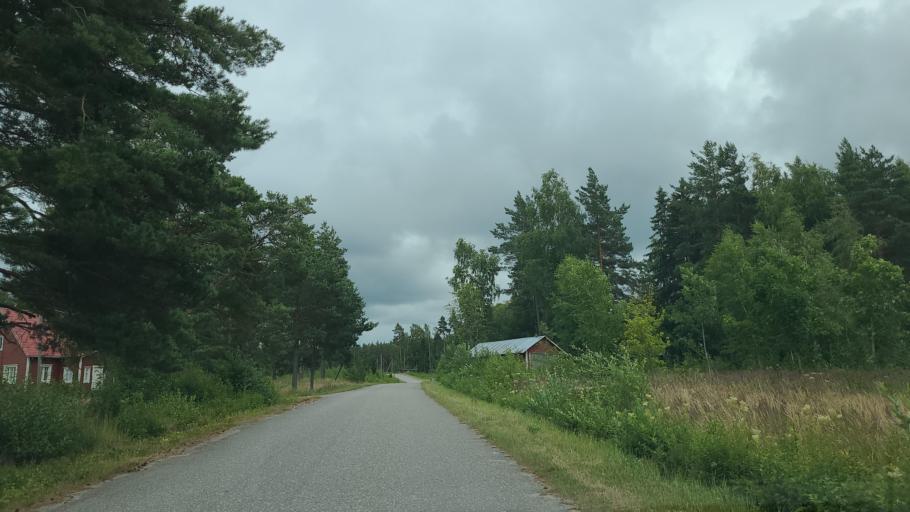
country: FI
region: Varsinais-Suomi
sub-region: Aboland-Turunmaa
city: Dragsfjaerd
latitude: 60.0821
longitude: 22.4136
